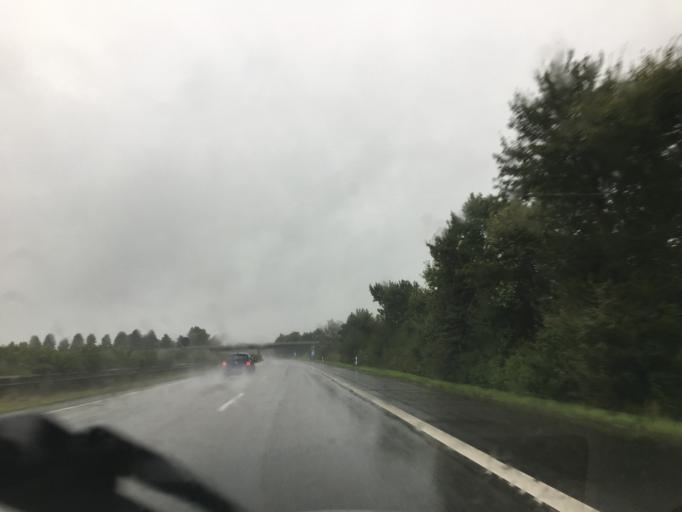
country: DE
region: Schleswig-Holstein
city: Rumohr
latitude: 54.2529
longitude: 10.0297
